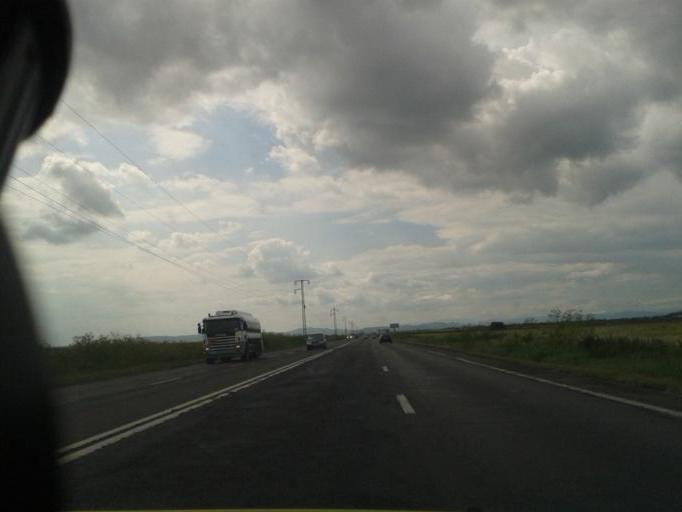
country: RO
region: Prahova
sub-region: Oras Baicoi
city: Liliesti
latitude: 45.0055
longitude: 25.8778
